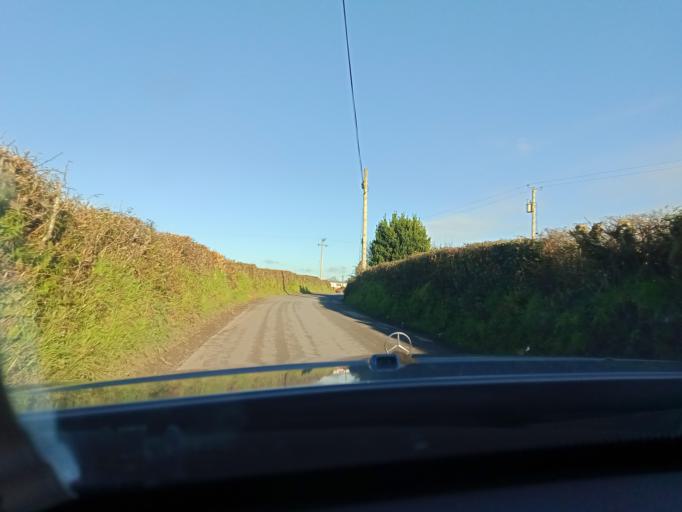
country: IE
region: Leinster
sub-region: Kilkenny
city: Mooncoin
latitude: 52.2881
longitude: -7.2336
